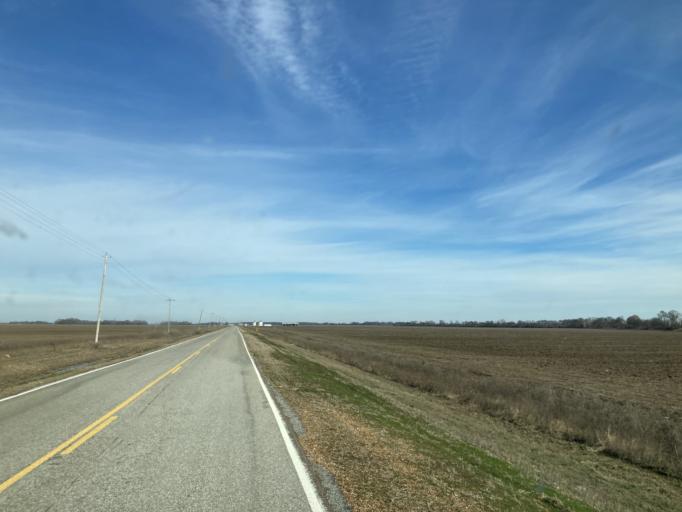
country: US
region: Mississippi
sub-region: Humphreys County
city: Belzoni
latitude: 32.9967
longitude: -90.6225
